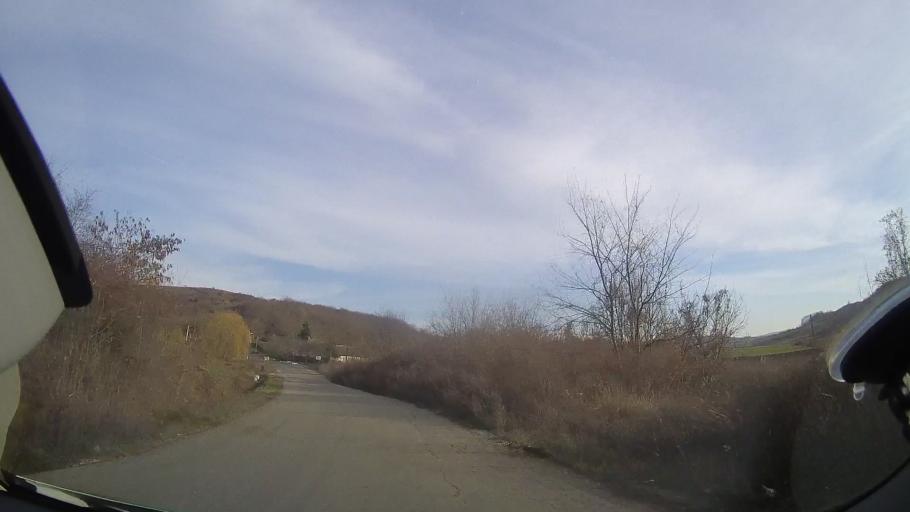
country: RO
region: Bihor
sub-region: Comuna Sarbi
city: Sarbi
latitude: 47.1792
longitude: 22.1395
